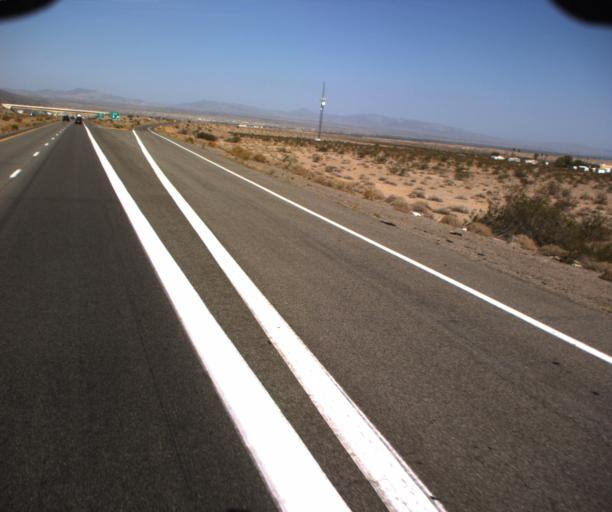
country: US
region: Arizona
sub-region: Mohave County
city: Desert Hills
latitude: 34.7230
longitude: -114.4296
